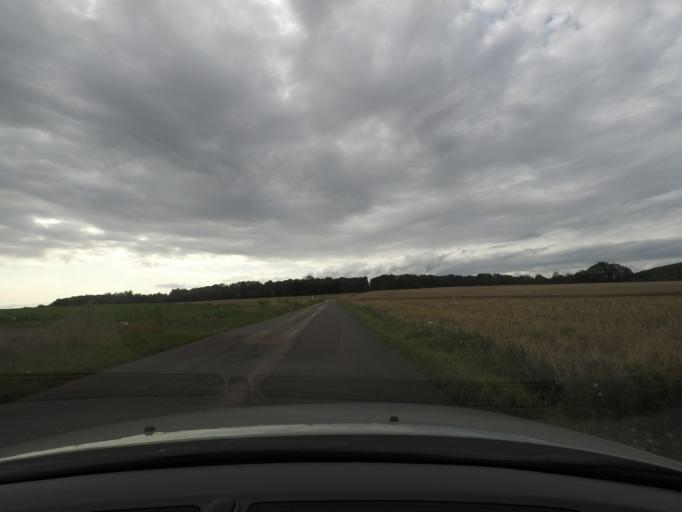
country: FR
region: Haute-Normandie
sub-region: Departement de l'Eure
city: Le Manoir
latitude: 49.3297
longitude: 1.2110
